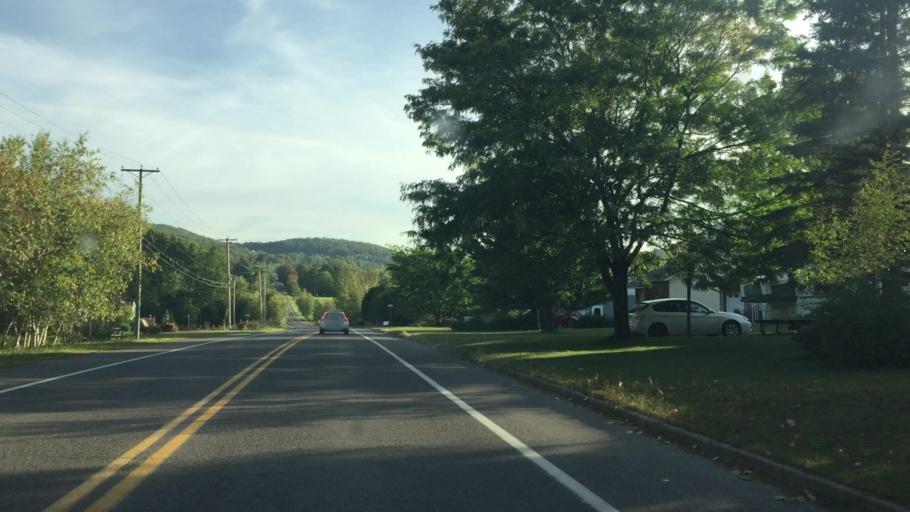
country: CA
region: Quebec
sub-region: Monteregie
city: Bromont
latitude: 45.3080
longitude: -72.6580
